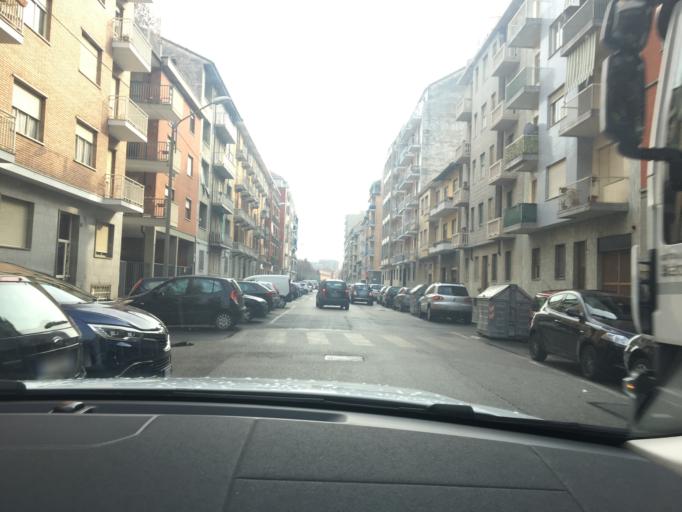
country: IT
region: Piedmont
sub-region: Provincia di Torino
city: Lesna
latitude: 45.0367
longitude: 7.6460
